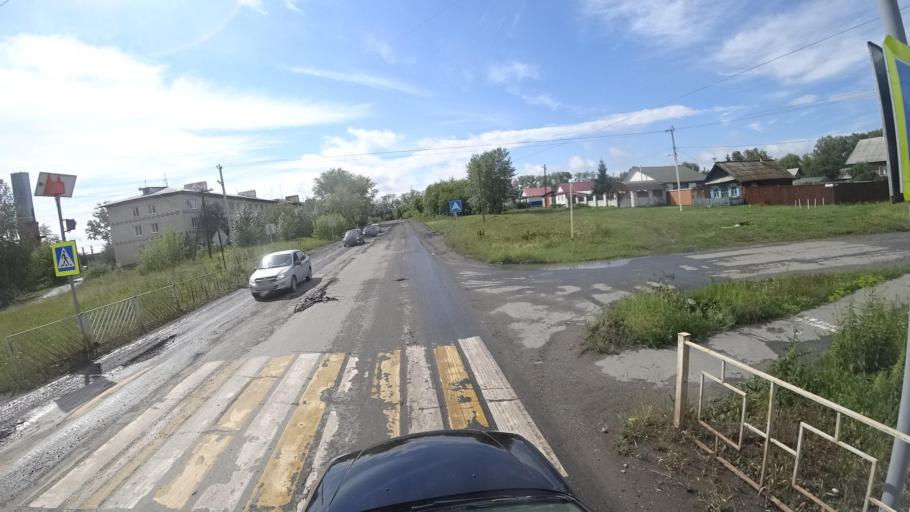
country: RU
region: Sverdlovsk
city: Kamyshlov
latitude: 56.8458
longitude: 62.7594
